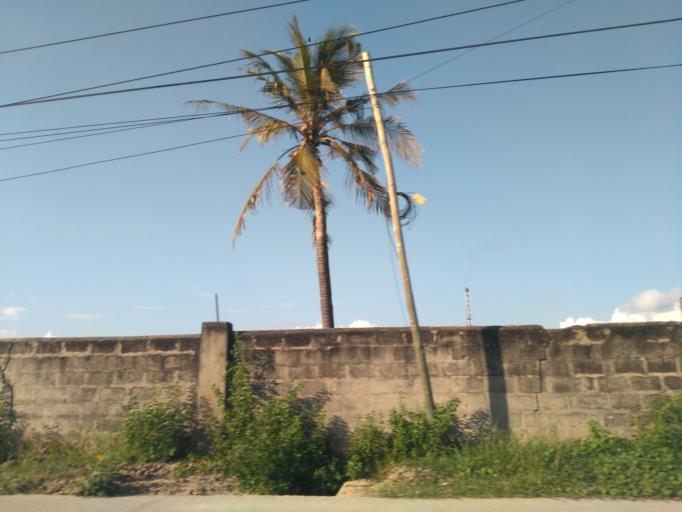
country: TZ
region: Dar es Salaam
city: Magomeni
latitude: -6.7597
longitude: 39.2376
